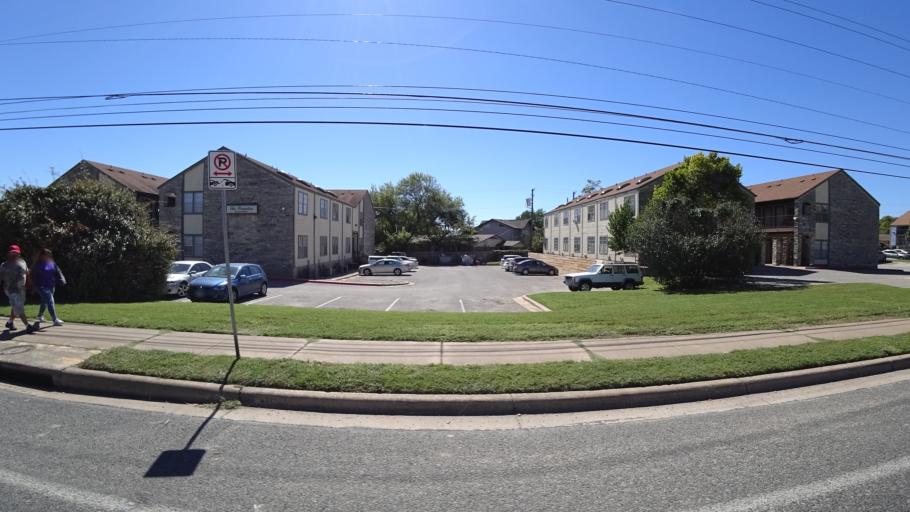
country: US
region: Texas
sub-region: Travis County
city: Austin
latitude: 30.2265
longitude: -97.7536
